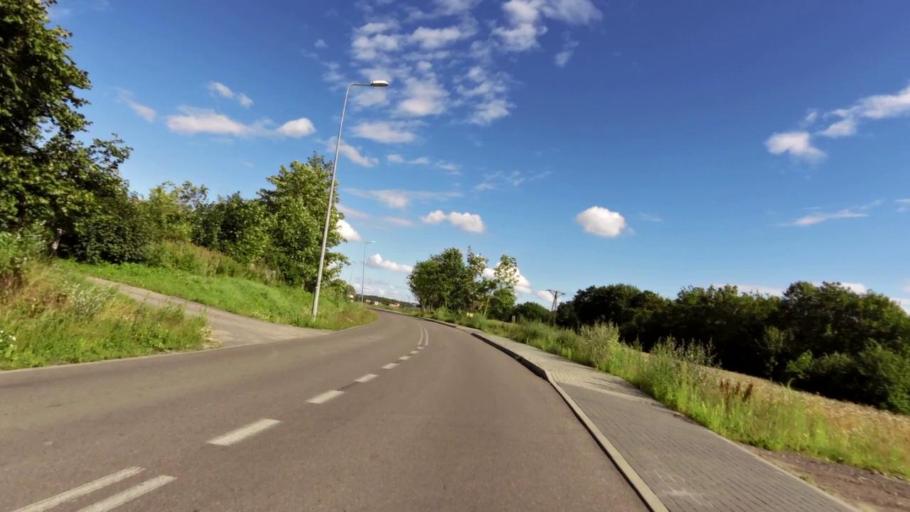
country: PL
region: West Pomeranian Voivodeship
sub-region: Powiat slawienski
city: Slawno
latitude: 54.4556
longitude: 16.7396
